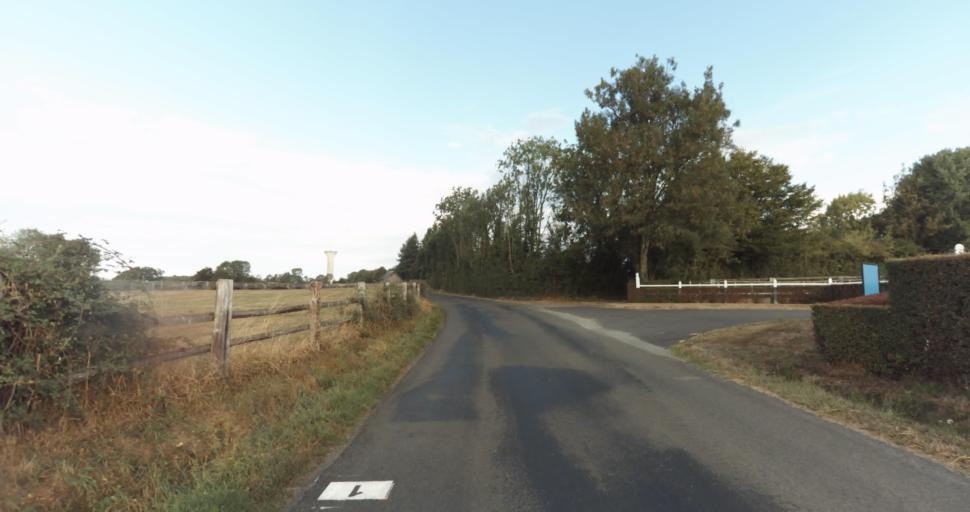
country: FR
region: Lower Normandy
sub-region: Departement de l'Orne
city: Vimoutiers
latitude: 48.9326
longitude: 0.2362
